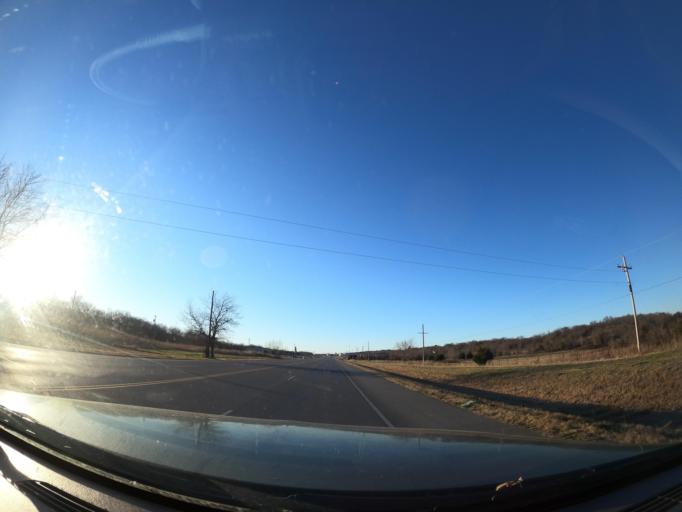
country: US
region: Oklahoma
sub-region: Pittsburg County
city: Krebs
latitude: 34.8951
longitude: -95.6682
